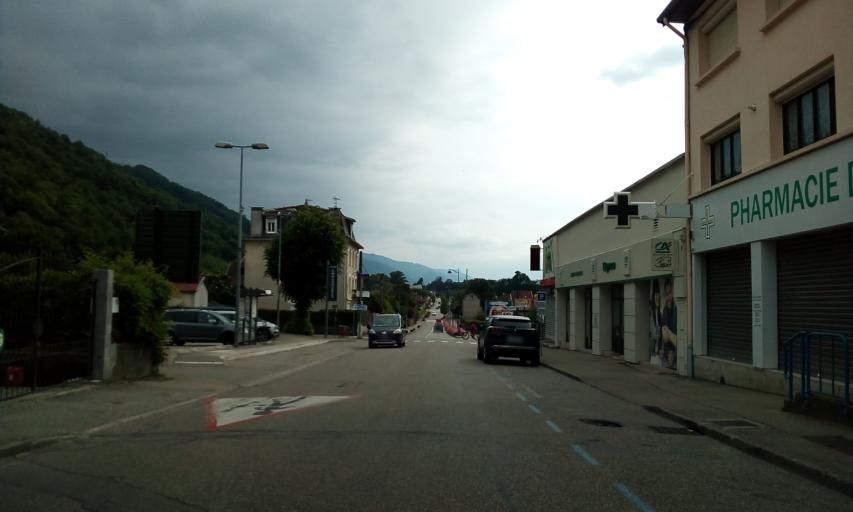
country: FR
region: Rhone-Alpes
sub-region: Departement de l'Isere
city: Froges
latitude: 45.2565
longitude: 5.9063
